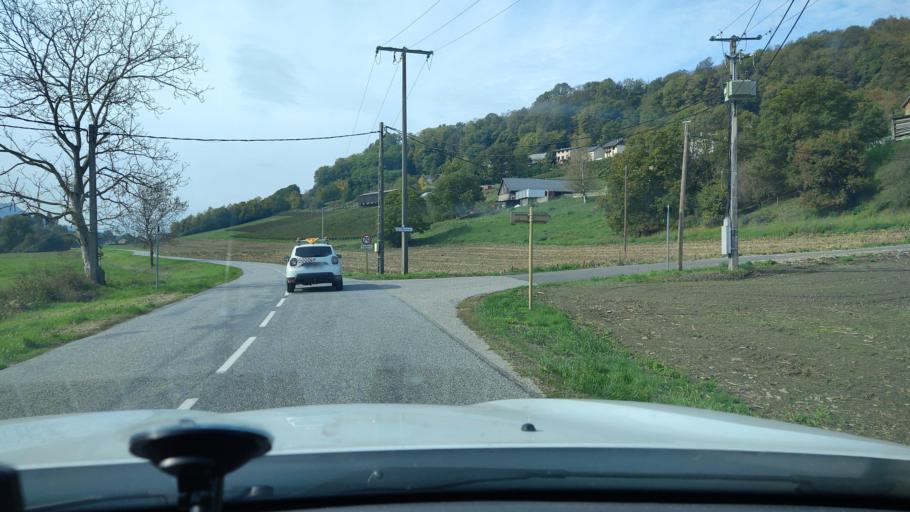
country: FR
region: Rhone-Alpes
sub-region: Departement de la Savoie
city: Coise-Saint-Jean-Pied-Gauthier
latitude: 45.5122
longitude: 6.1200
